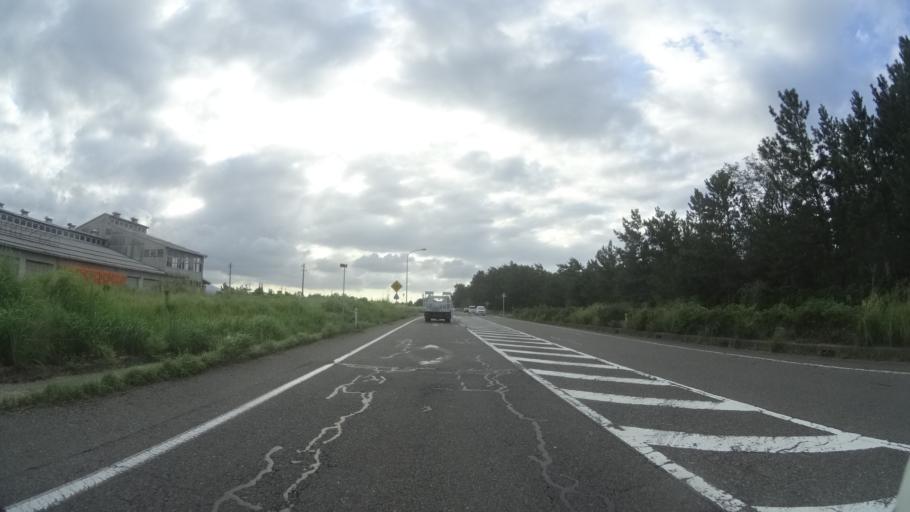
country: JP
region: Tottori
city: Kurayoshi
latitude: 35.4992
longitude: 133.7662
